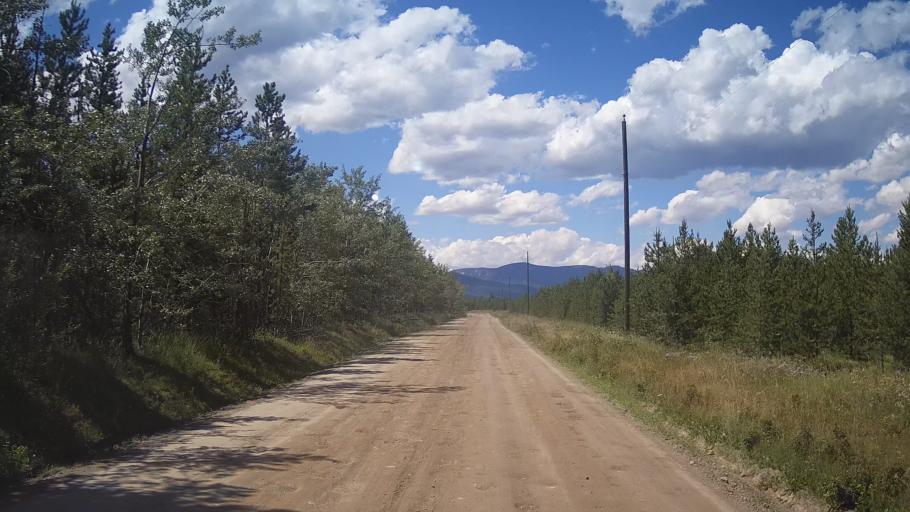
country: CA
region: British Columbia
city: Cache Creek
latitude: 51.2696
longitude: -121.7152
